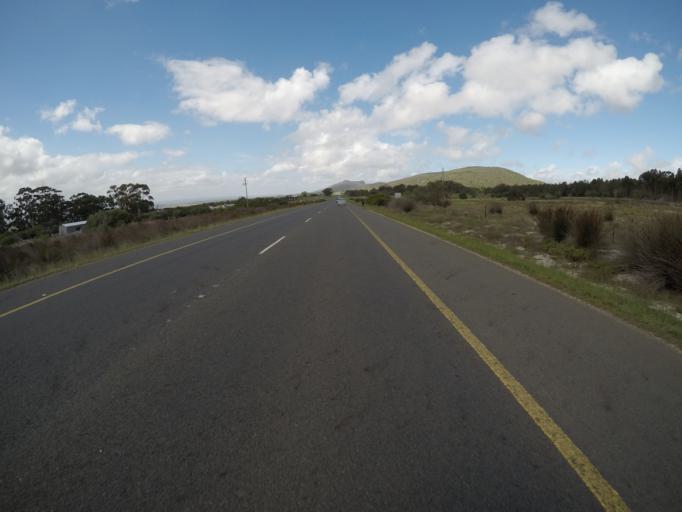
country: ZA
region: Western Cape
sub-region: Eden District Municipality
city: Riversdale
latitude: -34.2122
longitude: 21.5959
